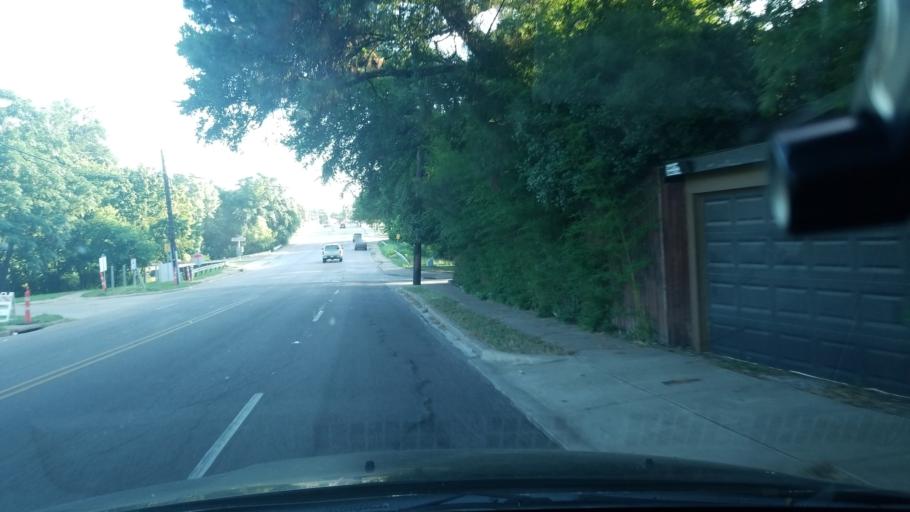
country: US
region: Texas
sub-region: Dallas County
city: Dallas
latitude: 32.7310
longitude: -96.8227
